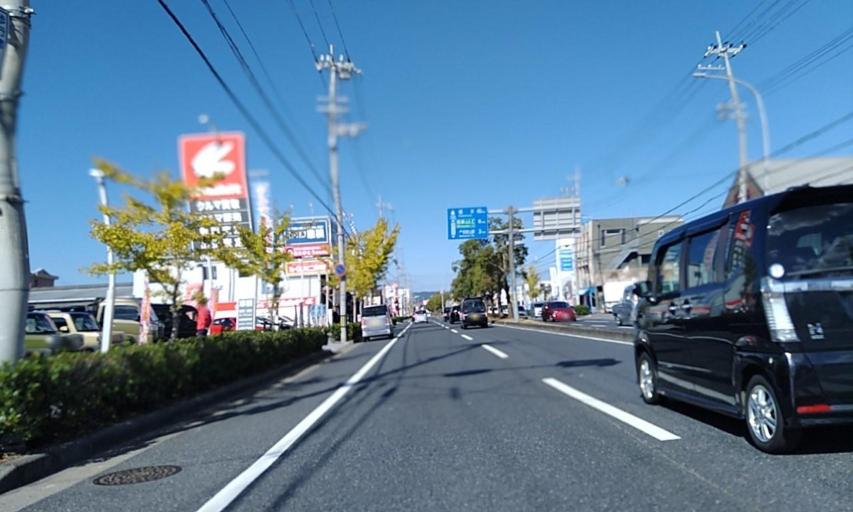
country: JP
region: Wakayama
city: Wakayama-shi
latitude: 34.2019
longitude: 135.1849
